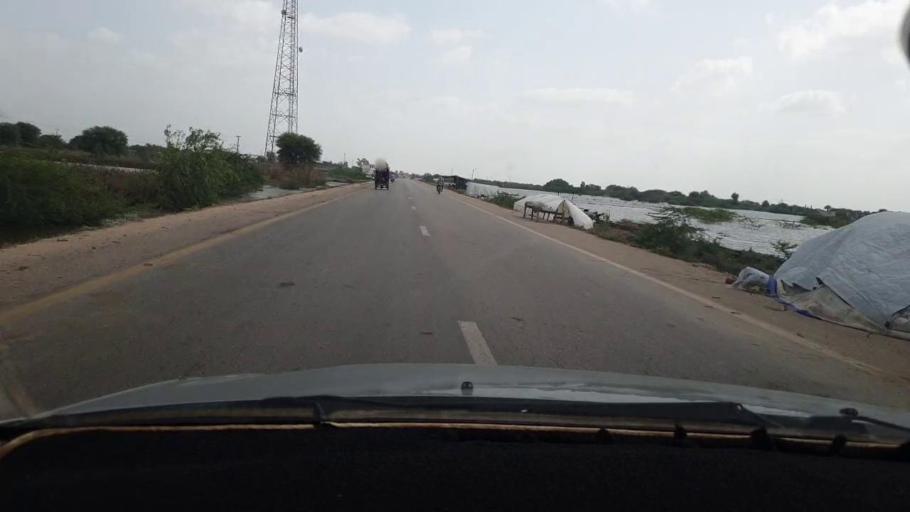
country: PK
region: Sindh
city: Naukot
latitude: 24.9920
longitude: 69.2914
